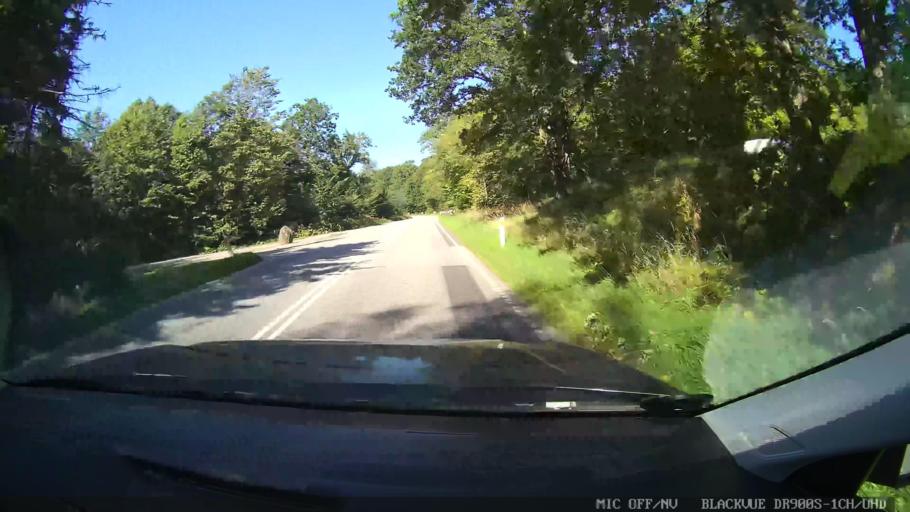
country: DK
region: North Denmark
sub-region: Mariagerfjord Kommune
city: Mariager
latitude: 56.6035
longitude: 9.9984
